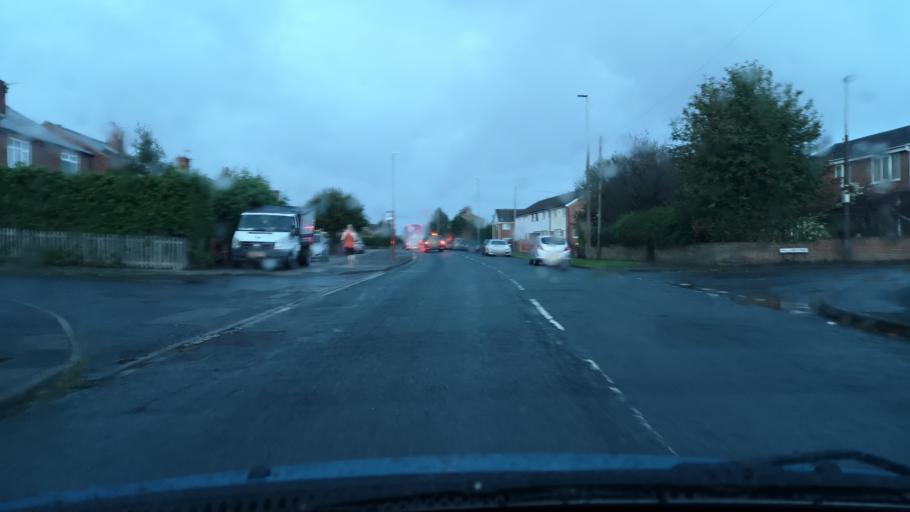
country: GB
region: England
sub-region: City and Borough of Leeds
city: Drighlington
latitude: 53.7348
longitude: -1.6483
